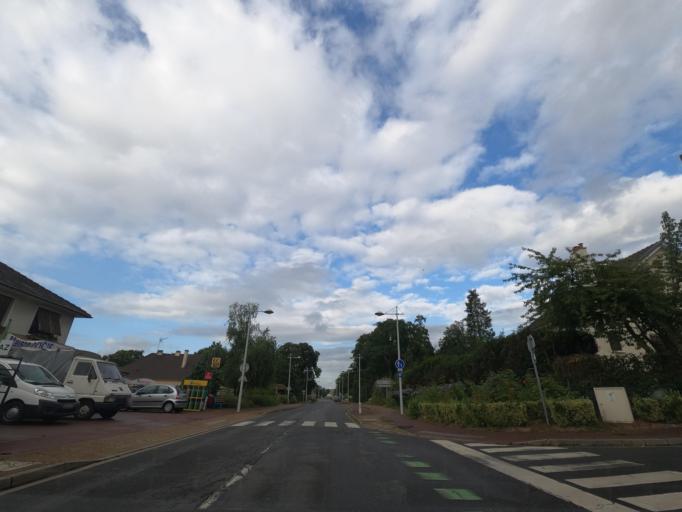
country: FR
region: Haute-Normandie
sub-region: Departement de la Seine-Maritime
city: Grand-Couronne
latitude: 49.3531
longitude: 1.0014
